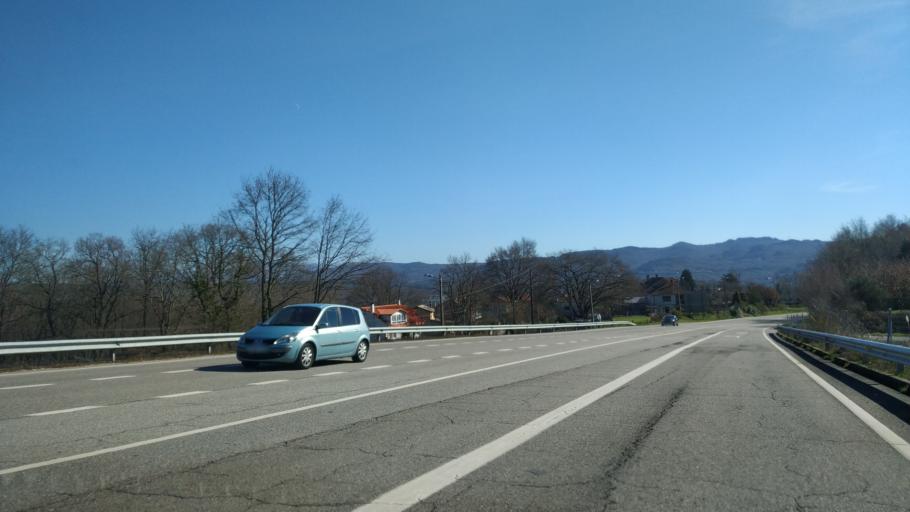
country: ES
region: Galicia
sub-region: Provincia de Ourense
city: Allariz
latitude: 42.2070
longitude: -7.8167
